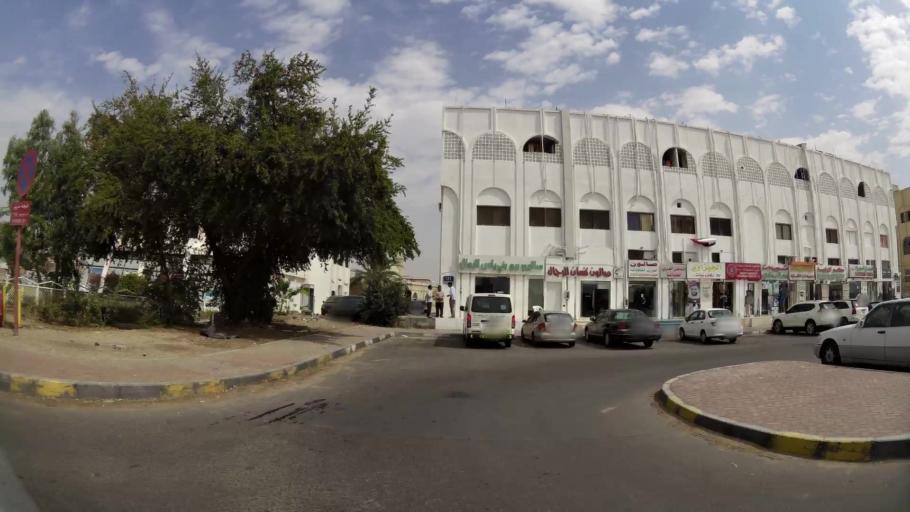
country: AE
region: Abu Dhabi
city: Abu Dhabi
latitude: 24.2968
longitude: 54.6284
